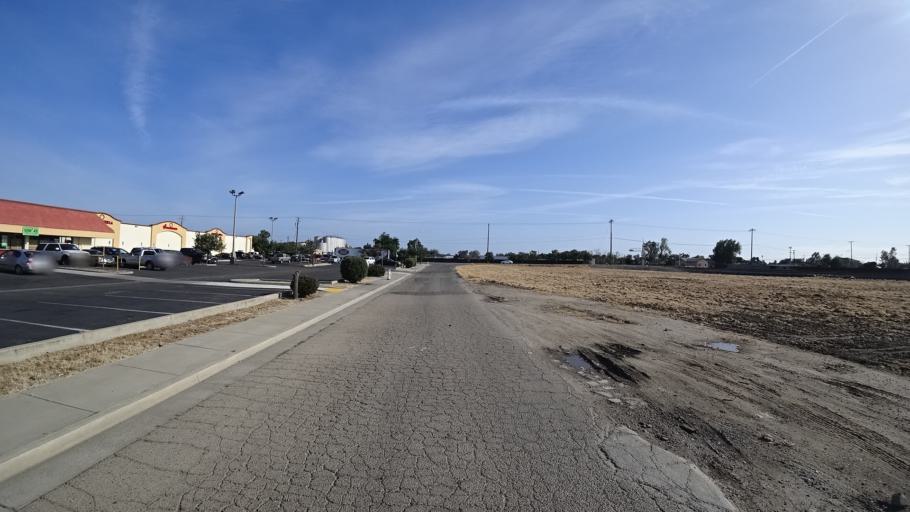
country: US
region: California
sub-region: Kings County
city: Hanford
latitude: 36.3122
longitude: -119.6506
